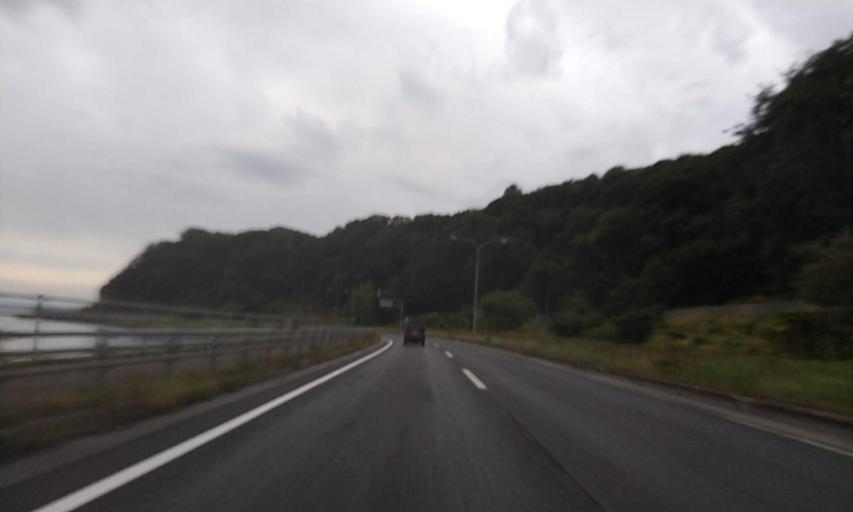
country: JP
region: Hokkaido
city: Abashiri
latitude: 44.0051
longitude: 144.2863
